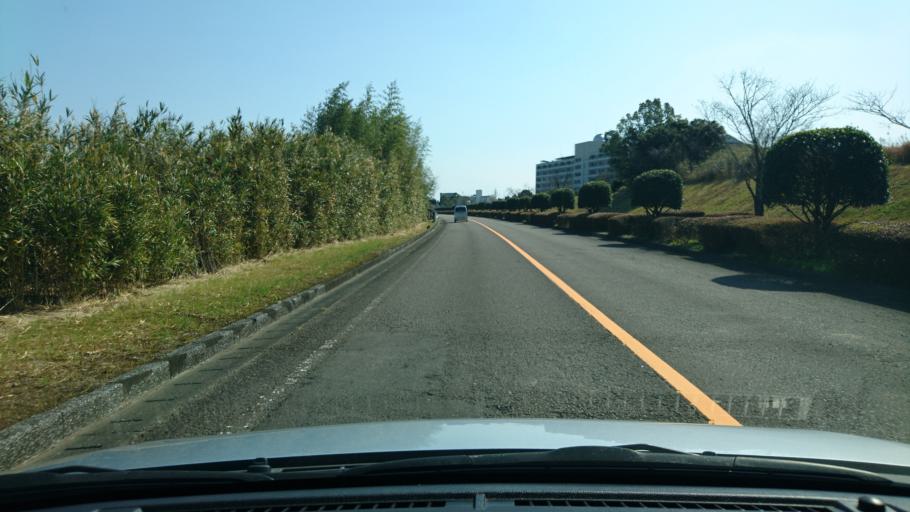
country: JP
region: Miyazaki
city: Miyazaki-shi
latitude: 31.8329
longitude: 131.4110
